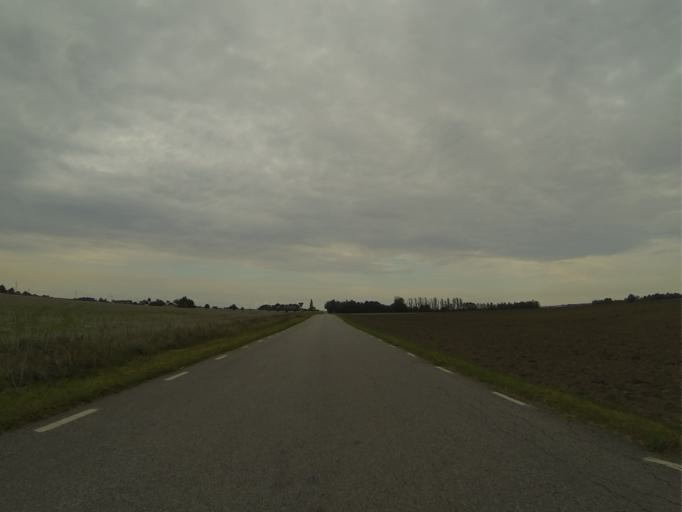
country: SE
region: Skane
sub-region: Staffanstorps Kommun
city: Hjaerup
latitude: 55.6428
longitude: 13.1492
